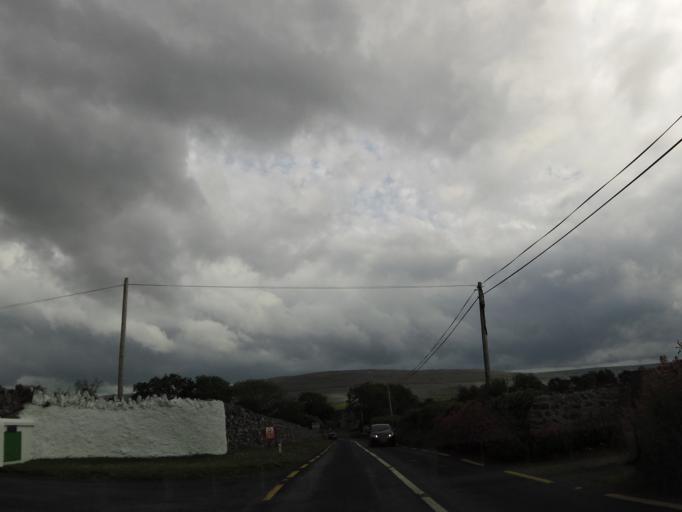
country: IE
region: Connaught
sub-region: County Galway
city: Bearna
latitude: 53.1248
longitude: -9.0788
